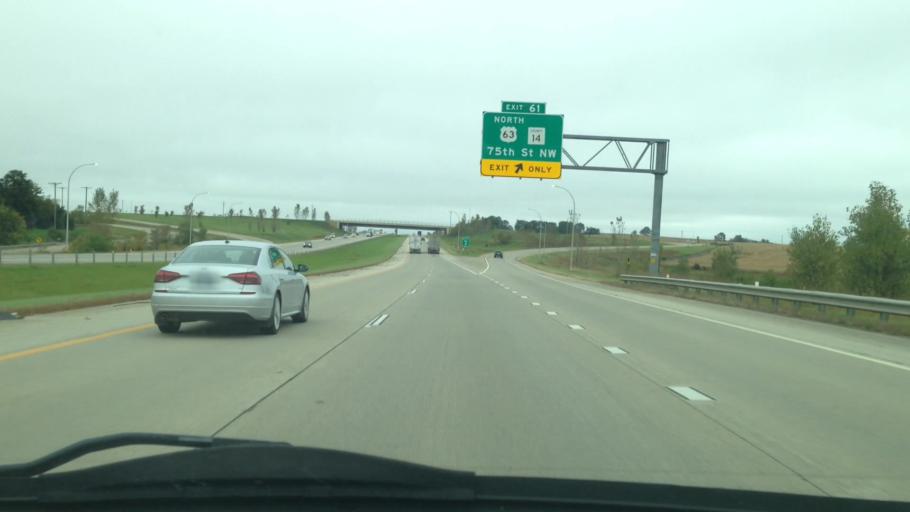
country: US
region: Minnesota
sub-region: Olmsted County
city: Oronoco
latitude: 44.1027
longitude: -92.5130
